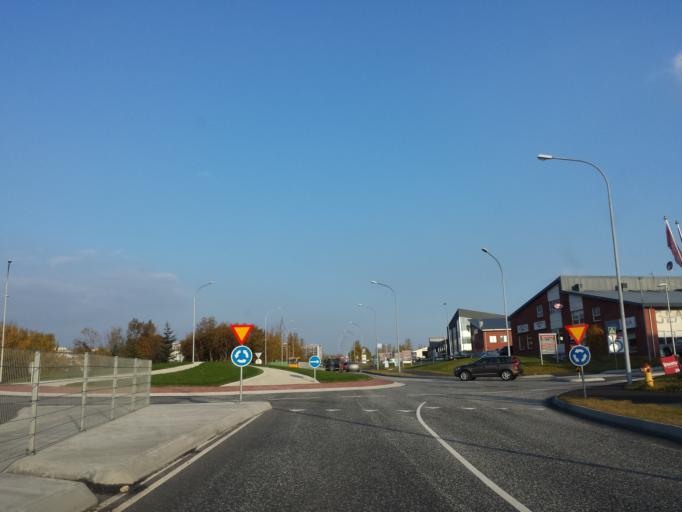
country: IS
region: Capital Region
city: Reykjavik
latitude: 64.1053
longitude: -21.8744
